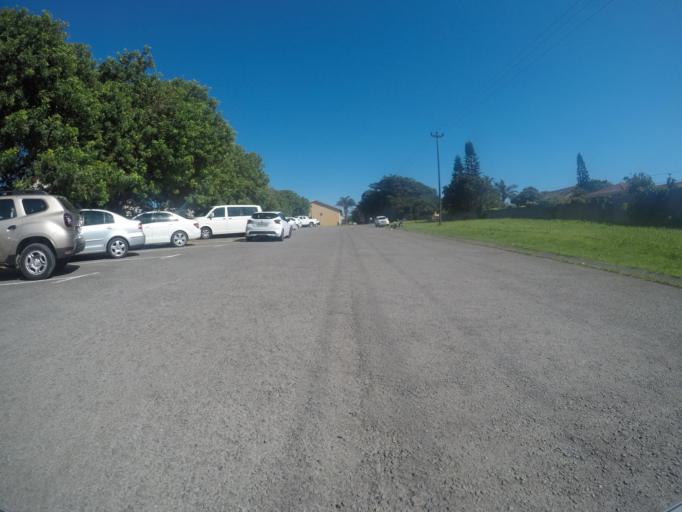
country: ZA
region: Eastern Cape
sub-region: Buffalo City Metropolitan Municipality
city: East London
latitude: -32.9411
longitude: 28.0038
